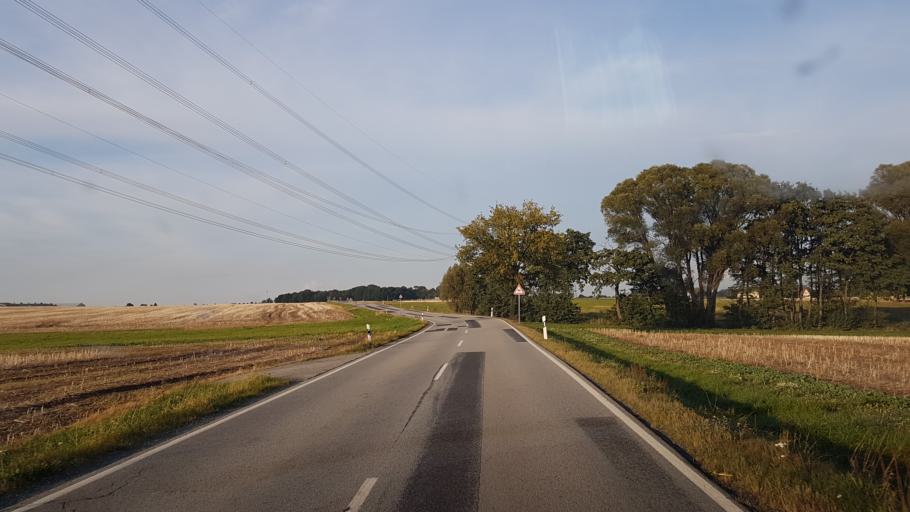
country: DE
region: Saxony
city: Panschwitz-Kuckau
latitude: 51.2014
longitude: 14.2224
